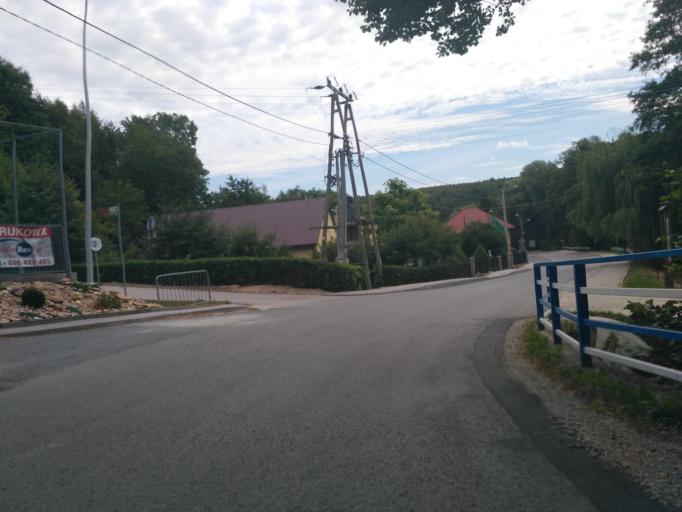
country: PL
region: Subcarpathian Voivodeship
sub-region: Powiat rzeszowski
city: Straszydle
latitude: 49.8994
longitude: 21.9496
